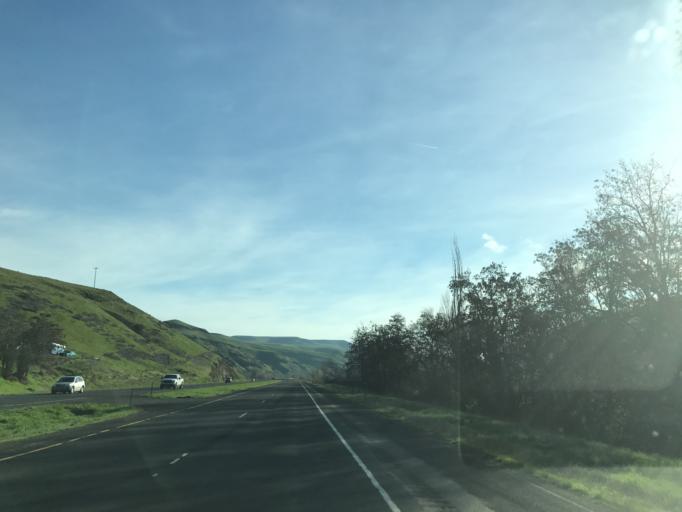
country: US
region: Idaho
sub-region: Nez Perce County
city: Lewiston Orchards
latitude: 46.4391
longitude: -116.8987
